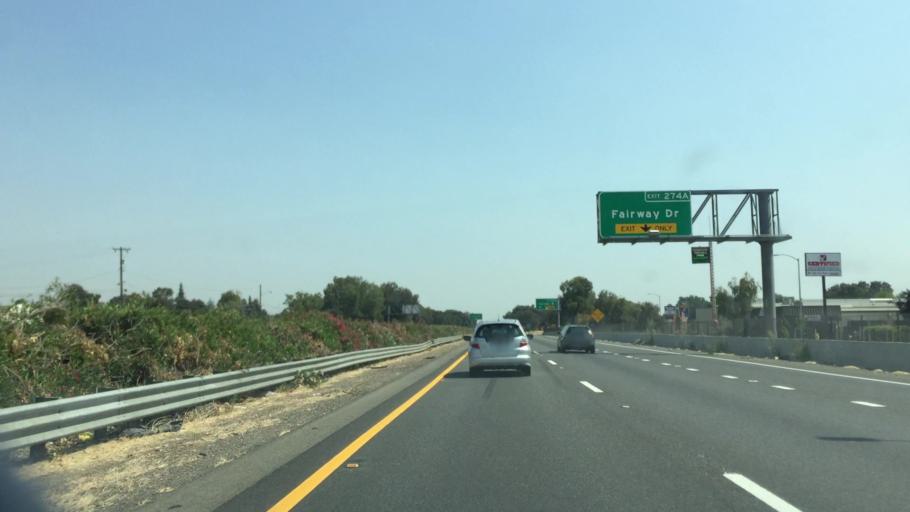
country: US
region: California
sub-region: Sacramento County
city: Galt
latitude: 38.2509
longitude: -121.2915
